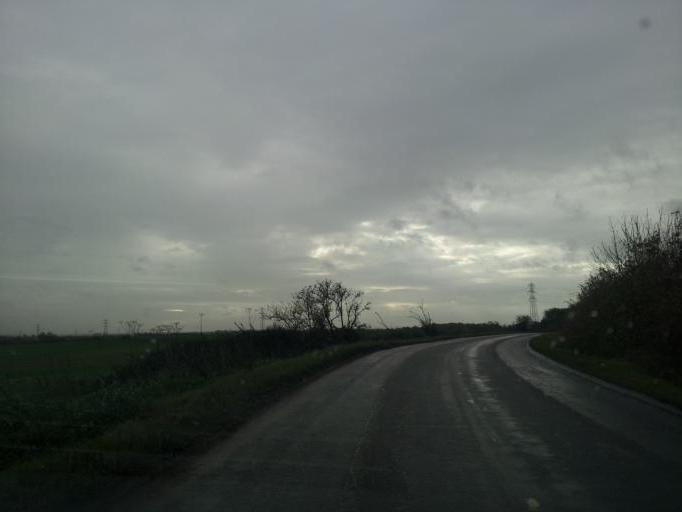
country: GB
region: England
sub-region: Nottinghamshire
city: Newark on Trent
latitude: 53.0235
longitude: -0.8025
